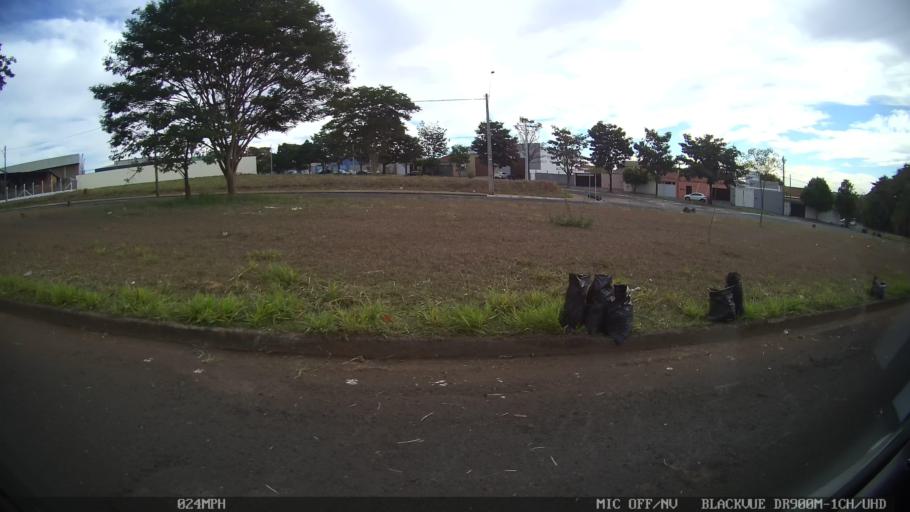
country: BR
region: Sao Paulo
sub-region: Catanduva
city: Catanduva
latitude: -21.1506
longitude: -48.9952
